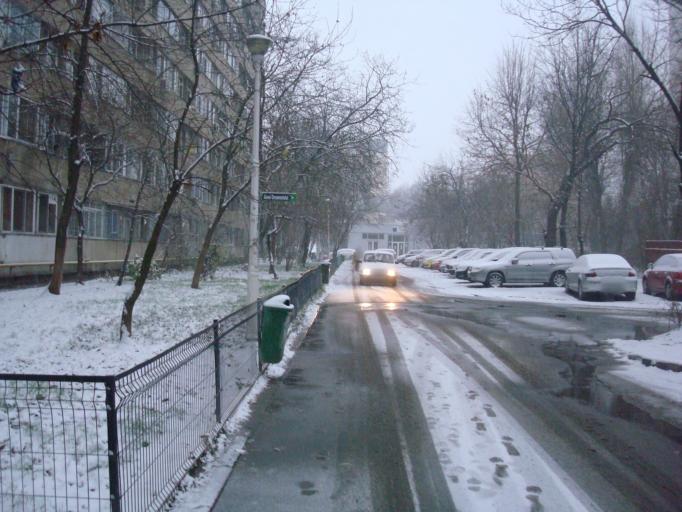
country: RO
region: Ilfov
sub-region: Comuna Popesti-Leordeni
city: Popesti-Leordeni
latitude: 44.3797
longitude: 26.1257
